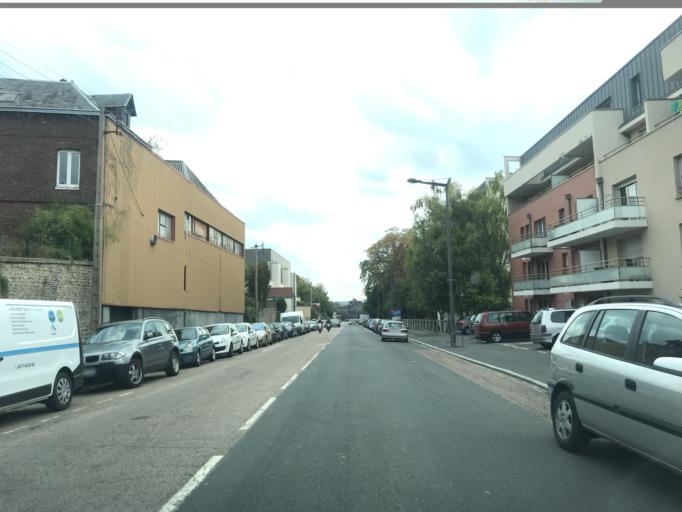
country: FR
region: Haute-Normandie
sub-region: Departement de la Seine-Maritime
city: Deville-les-Rouen
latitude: 49.4572
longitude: 1.0559
